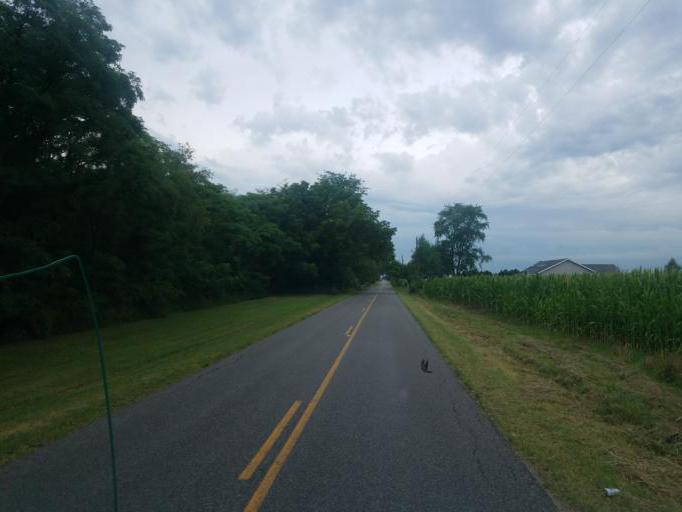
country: US
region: Ohio
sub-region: Paulding County
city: Antwerp
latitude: 41.2375
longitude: -84.7147
